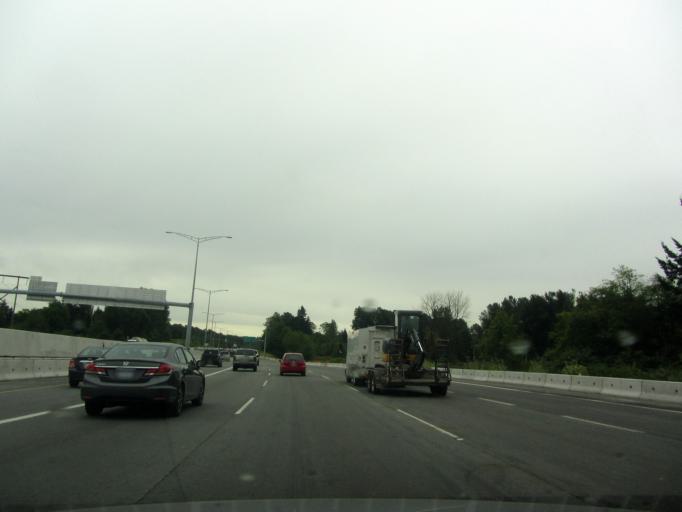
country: CA
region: British Columbia
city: Burnaby
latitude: 49.2577
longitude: -122.9962
